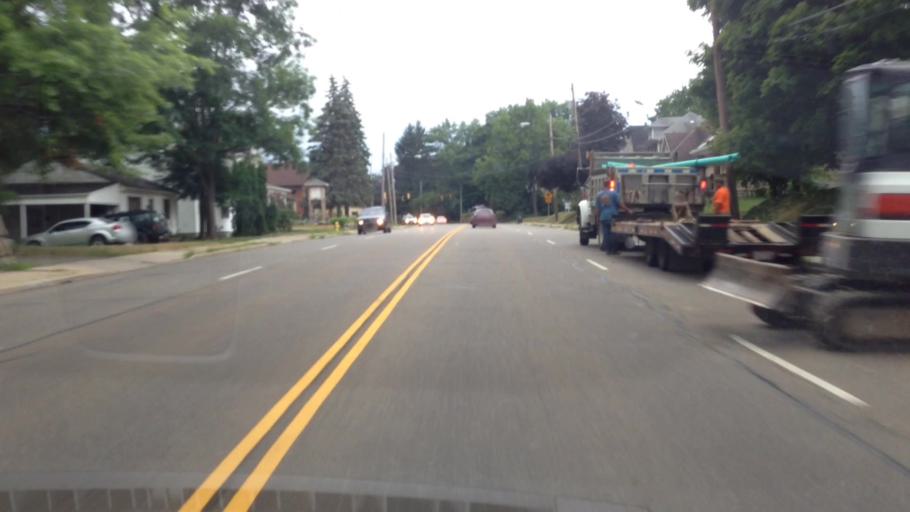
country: US
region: Ohio
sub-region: Summit County
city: Barberton
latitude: 41.0329
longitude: -81.5885
